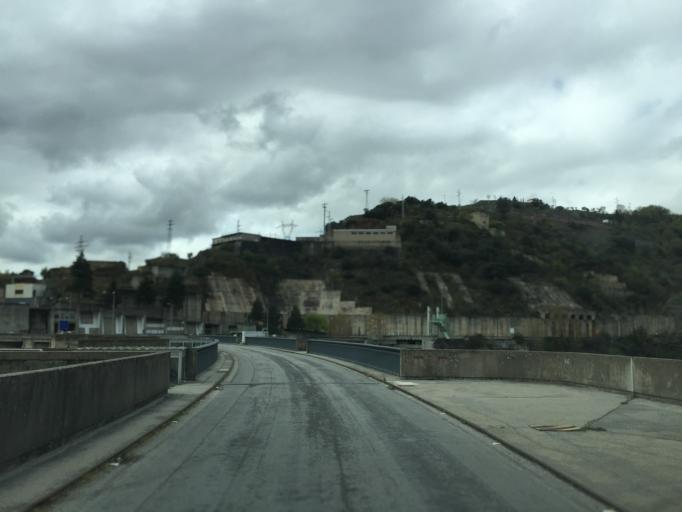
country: PT
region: Braganca
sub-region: Miranda do Douro
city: Miranda do Douro
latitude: 41.4900
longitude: -6.2631
